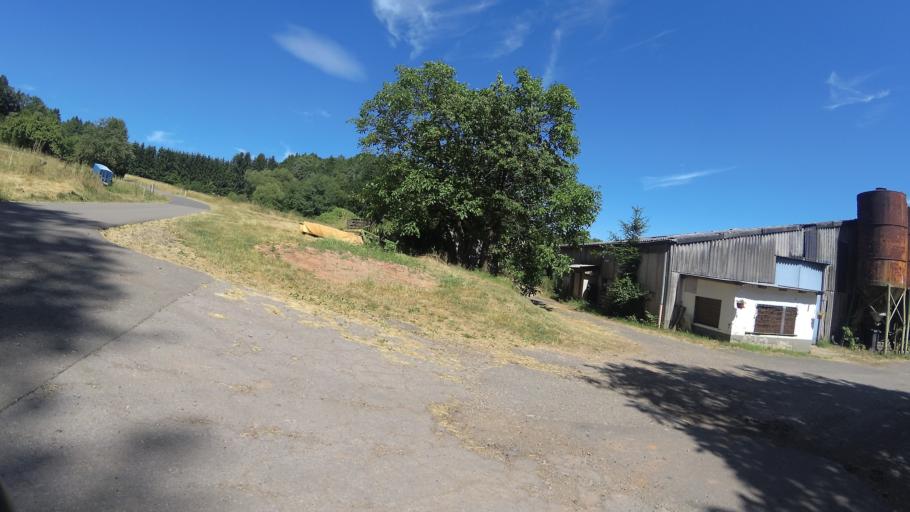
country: DE
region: Saarland
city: Namborn
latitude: 49.4947
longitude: 7.1303
